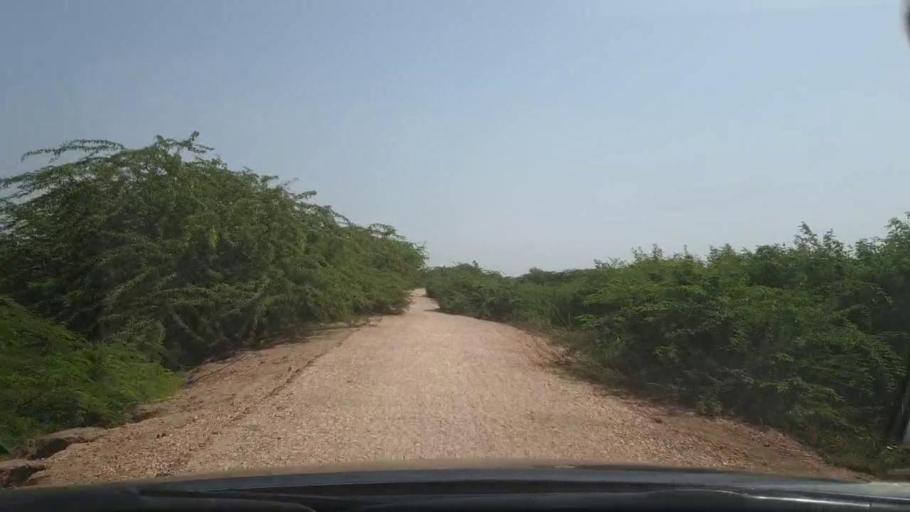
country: PK
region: Sindh
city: Tando Bago
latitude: 24.7994
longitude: 69.1591
